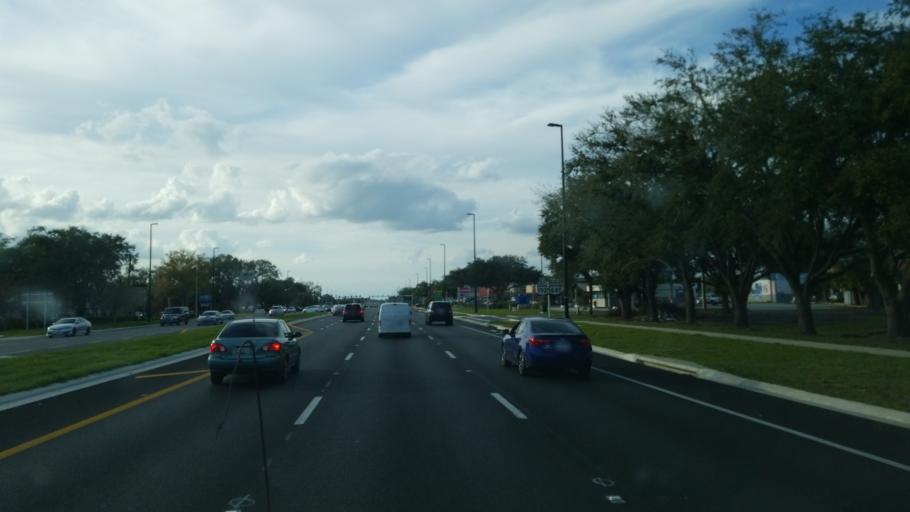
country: US
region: Florida
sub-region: Osceola County
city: Saint Cloud
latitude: 28.2492
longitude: -81.3107
